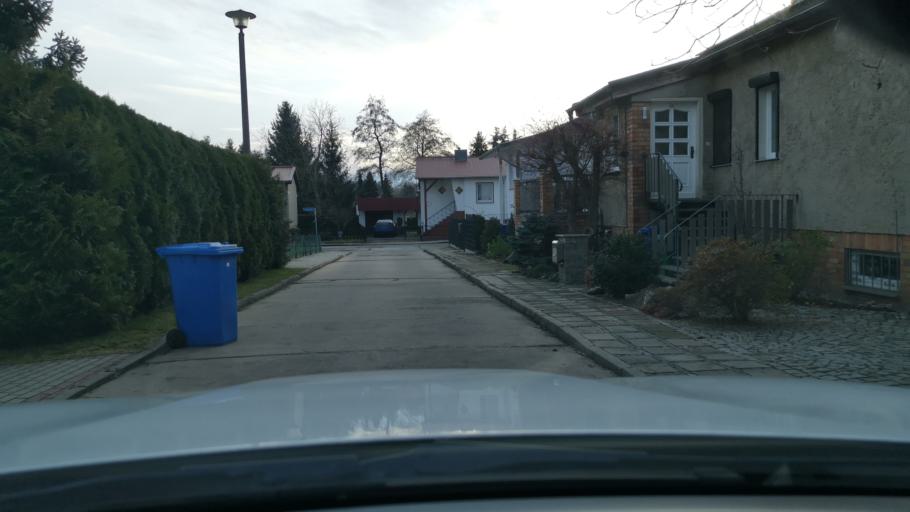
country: DE
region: Brandenburg
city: Juterbog
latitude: 51.9992
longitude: 13.0925
